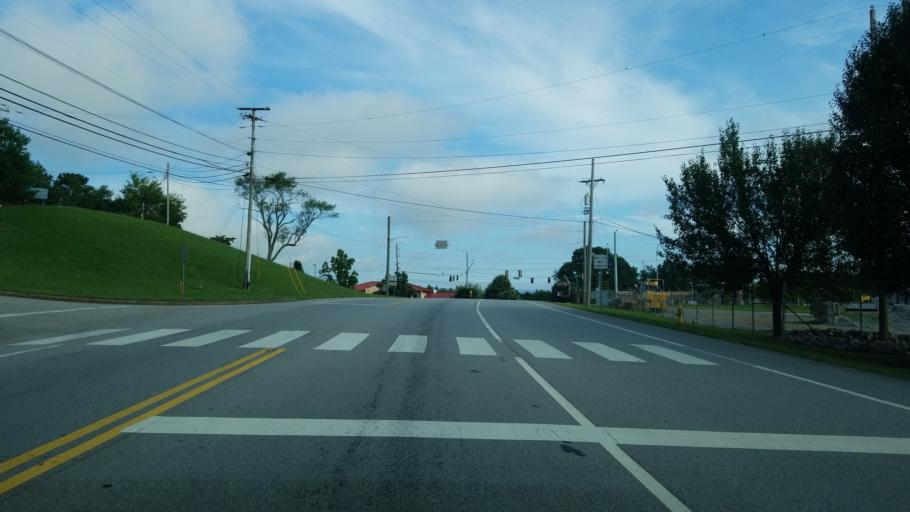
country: US
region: Tennessee
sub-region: Hamilton County
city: East Chattanooga
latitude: 35.0803
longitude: -85.2090
